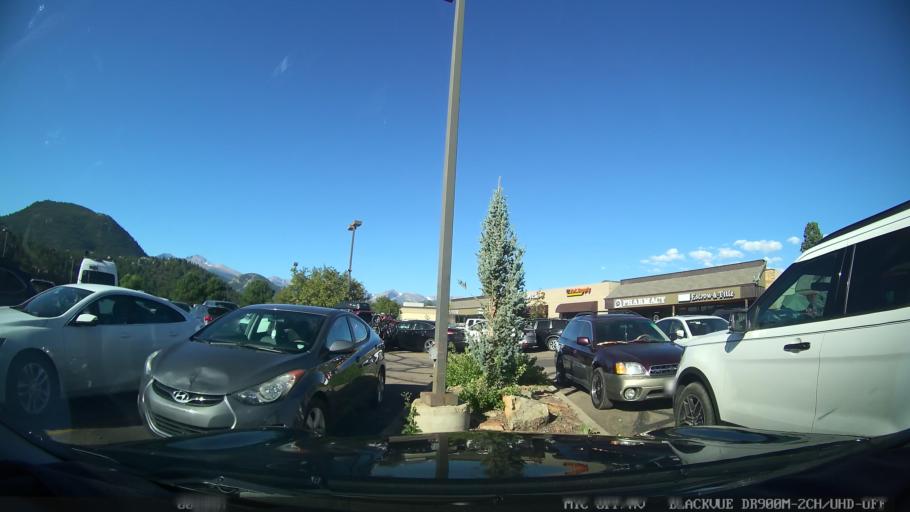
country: US
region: Colorado
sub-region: Larimer County
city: Estes Park
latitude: 40.3809
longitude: -105.5149
